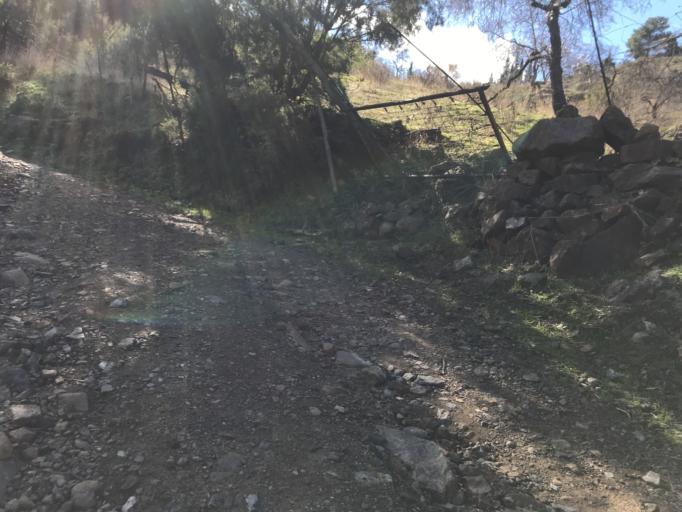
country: ES
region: Andalusia
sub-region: Provincia de Malaga
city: Tolox
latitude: 36.6748
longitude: -4.9153
